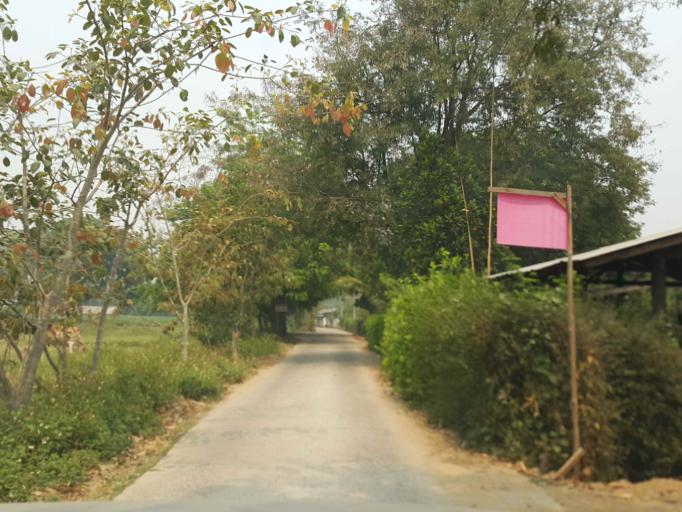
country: TH
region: Chiang Mai
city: Mae Taeng
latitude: 19.0729
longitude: 98.9400
